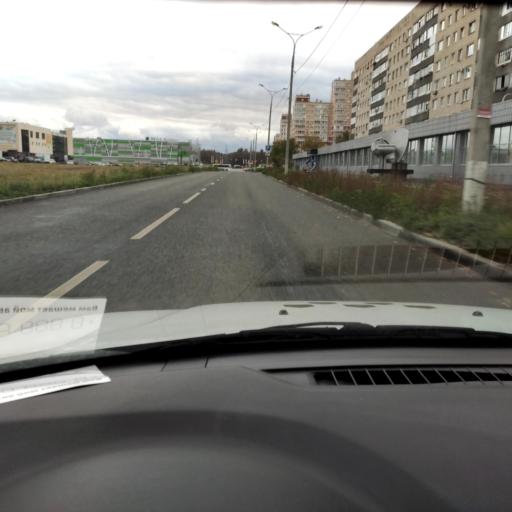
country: RU
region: Samara
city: Tol'yatti
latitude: 53.5030
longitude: 49.4206
